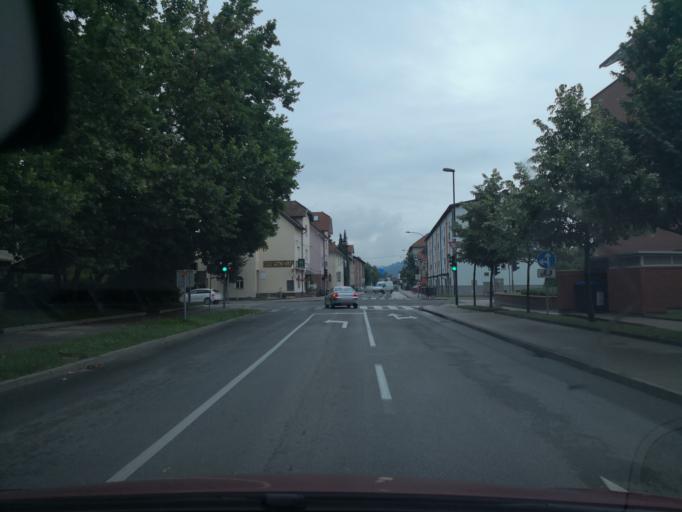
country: SI
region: Ljubljana
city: Ljubljana
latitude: 46.0636
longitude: 14.5311
